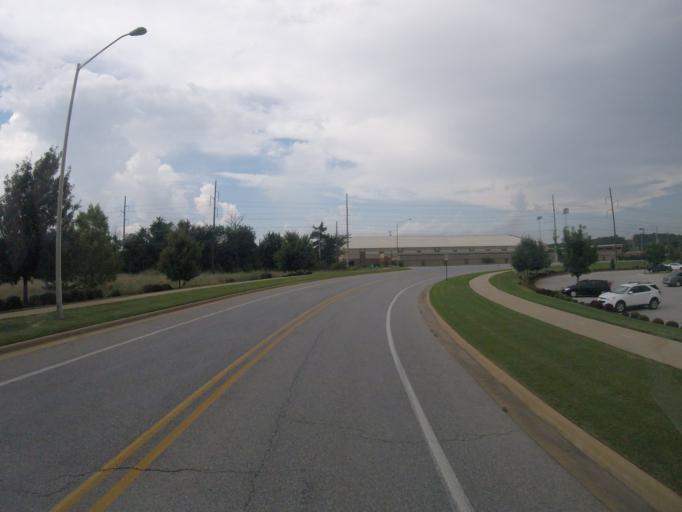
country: US
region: Arkansas
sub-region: Washington County
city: Fayetteville
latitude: 36.0481
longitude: -94.1851
